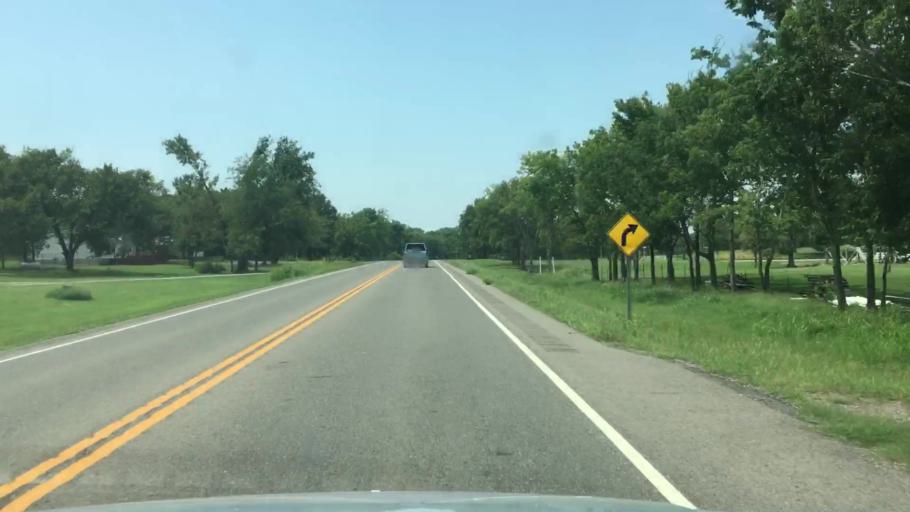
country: US
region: Oklahoma
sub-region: Wagoner County
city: Wagoner
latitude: 35.9378
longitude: -95.3126
